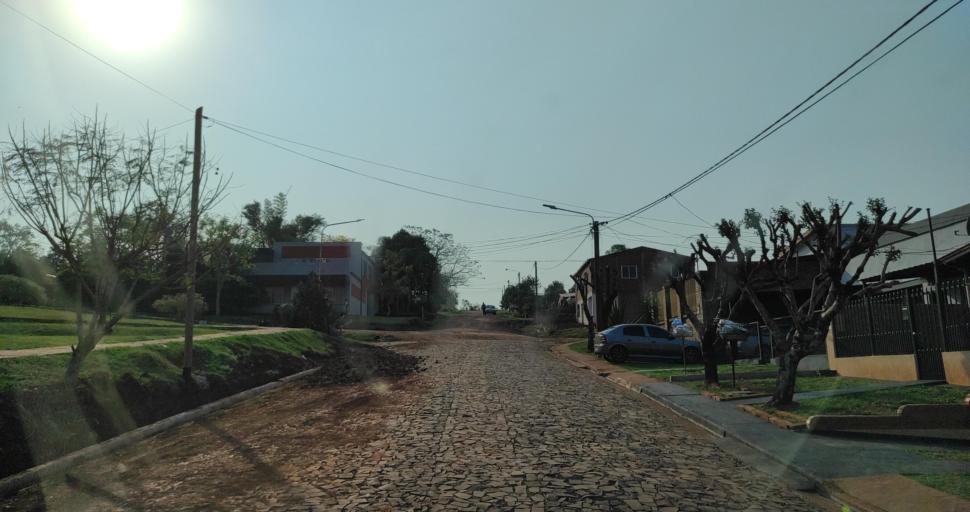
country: AR
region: Misiones
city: Cerro Azul
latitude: -27.6295
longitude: -55.4960
